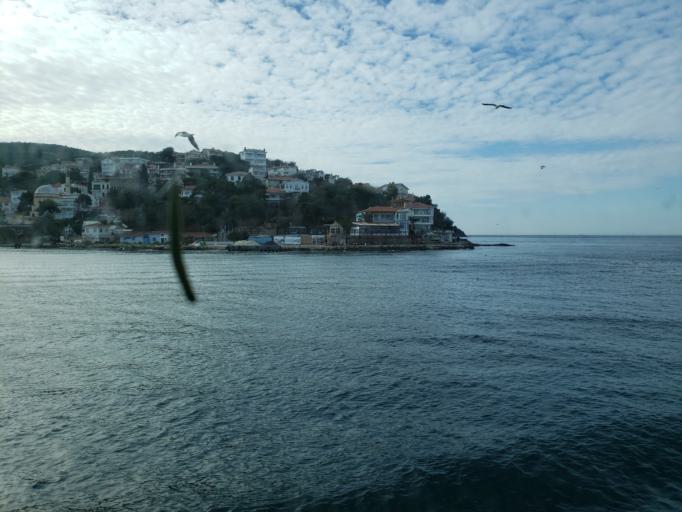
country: TR
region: Istanbul
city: Adalan
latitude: 40.8842
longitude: 29.0715
